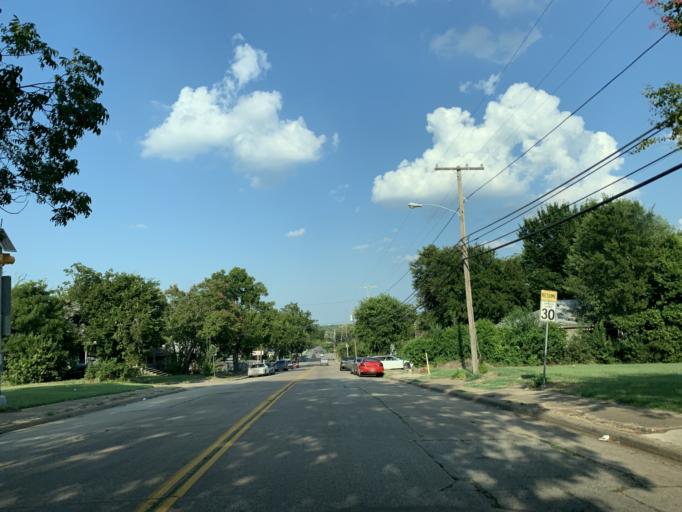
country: US
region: Texas
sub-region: Dallas County
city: Dallas
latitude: 32.7415
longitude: -96.7910
